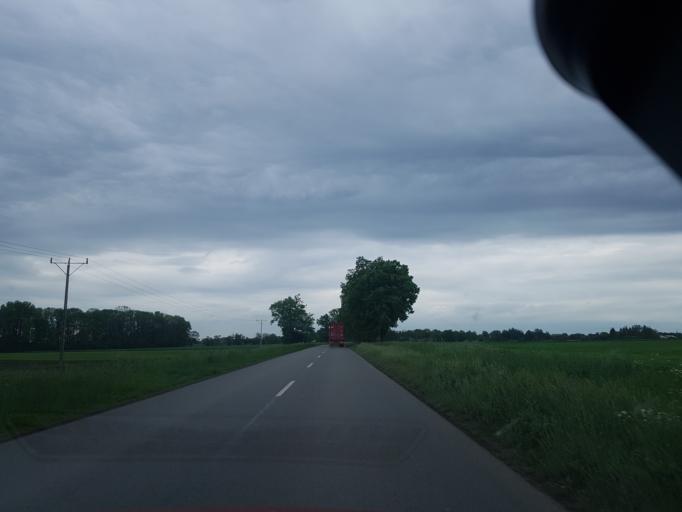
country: PL
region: Lower Silesian Voivodeship
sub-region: Powiat wroclawski
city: Zorawina
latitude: 50.9237
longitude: 17.0230
